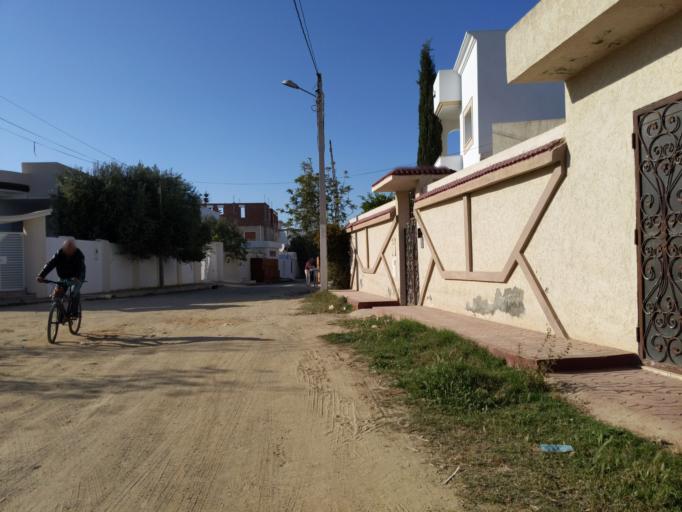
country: TN
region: Al Munastir
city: Saqanis
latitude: 35.7758
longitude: 10.7990
